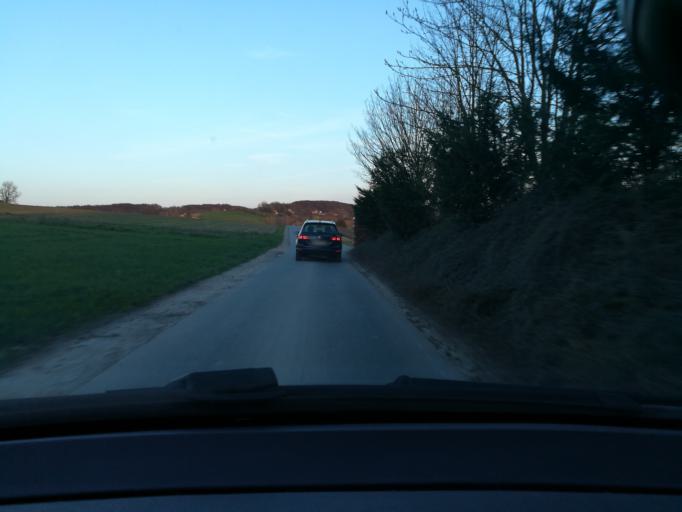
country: DE
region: North Rhine-Westphalia
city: Halle
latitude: 52.0915
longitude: 8.3419
